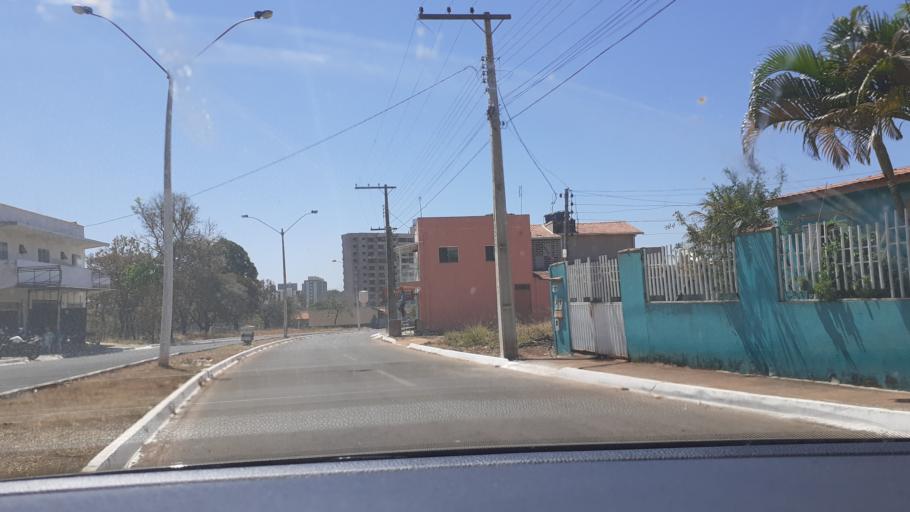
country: BR
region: Goias
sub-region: Caldas Novas
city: Caldas Novas
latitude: -17.7400
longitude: -48.6405
